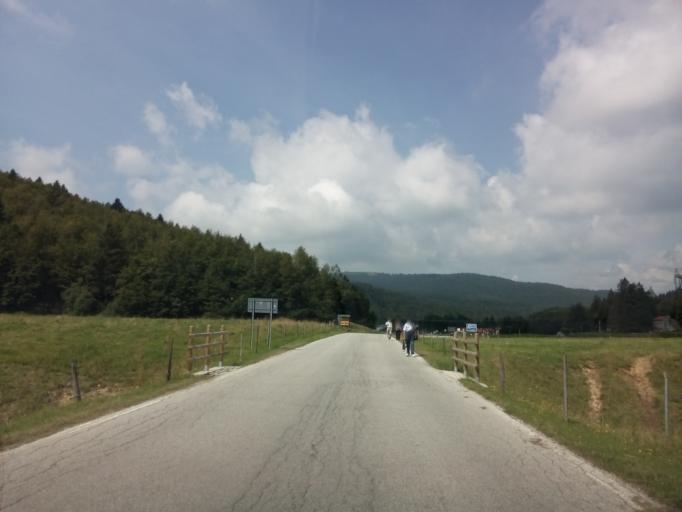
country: IT
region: Veneto
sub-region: Provincia di Vicenza
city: Conco
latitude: 45.8214
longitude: 11.6204
